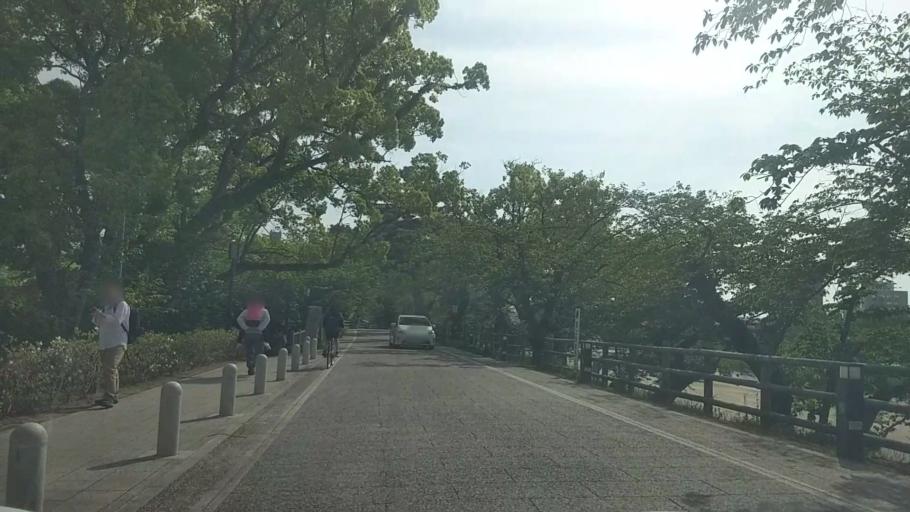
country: JP
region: Aichi
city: Okazaki
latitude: 34.9551
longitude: 137.1589
